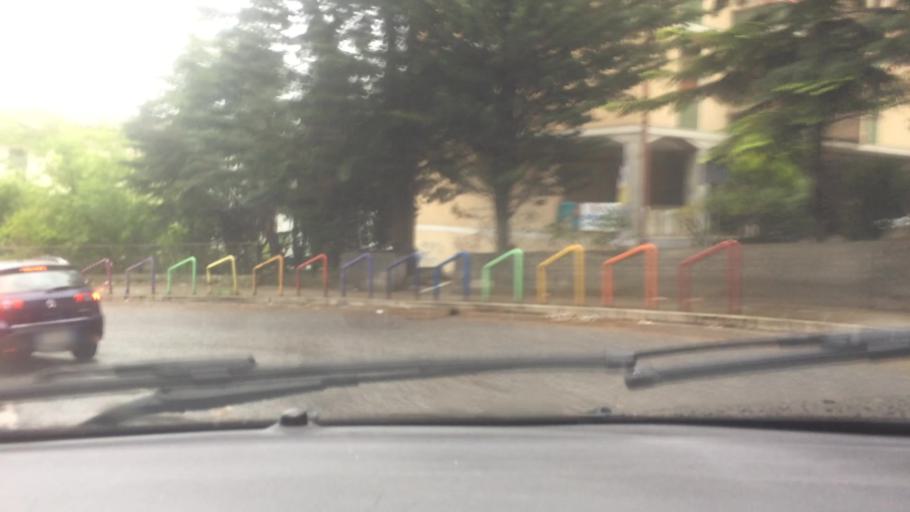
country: IT
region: Basilicate
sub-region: Provincia di Potenza
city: Potenza
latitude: 40.6450
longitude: 15.7961
